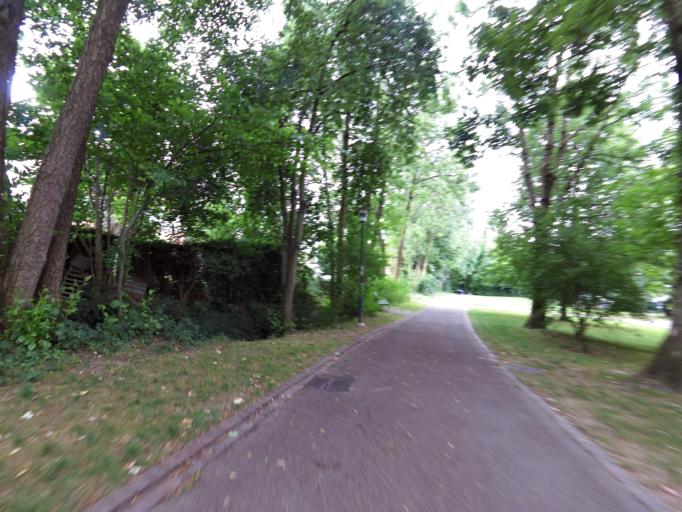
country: CH
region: Zurich
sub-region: Bezirk Zuerich
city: Zuerich (Kreis 10) / Ruetihof
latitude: 47.4067
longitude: 8.4858
